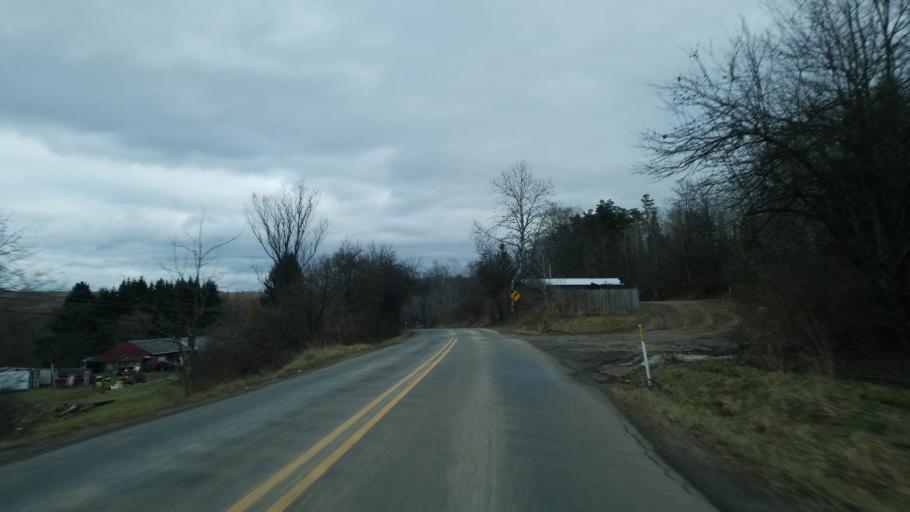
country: US
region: Pennsylvania
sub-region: Jefferson County
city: Falls Creek
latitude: 41.1174
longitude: -78.8076
